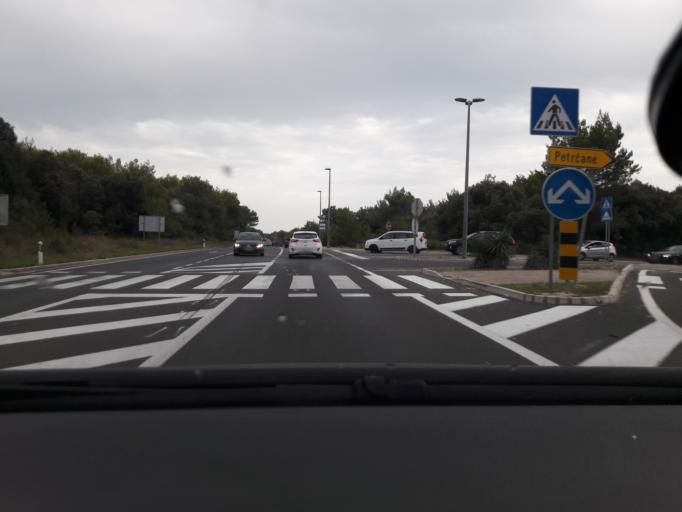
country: HR
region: Zadarska
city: Nin
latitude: 44.1932
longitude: 15.1786
